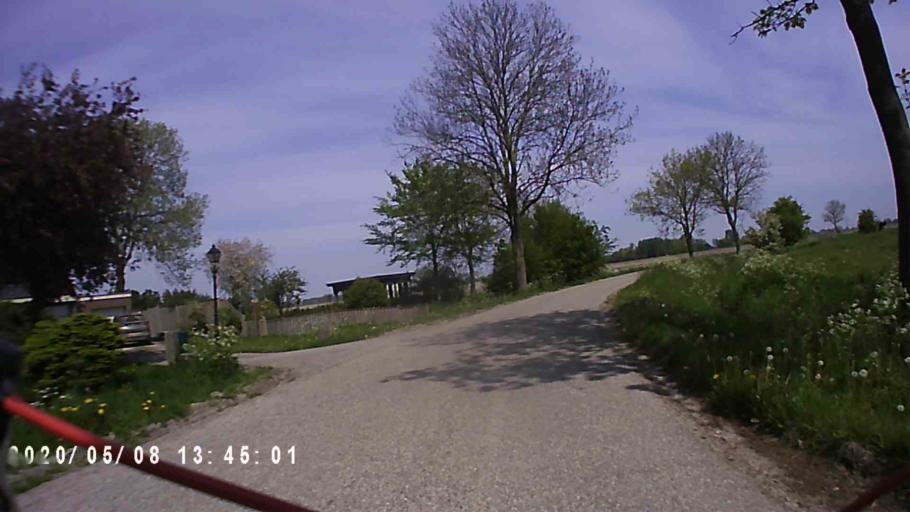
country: NL
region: Groningen
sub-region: Gemeente Appingedam
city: Appingedam
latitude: 53.3264
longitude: 6.7865
